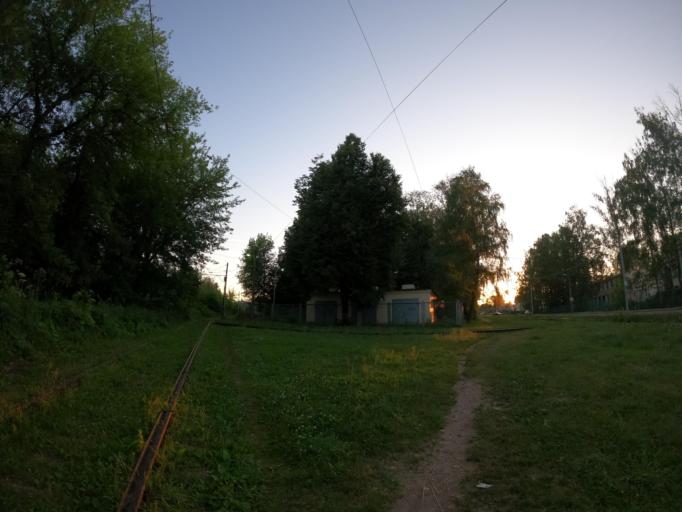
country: RU
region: Moskovskaya
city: Kolomna
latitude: 55.0737
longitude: 38.7865
